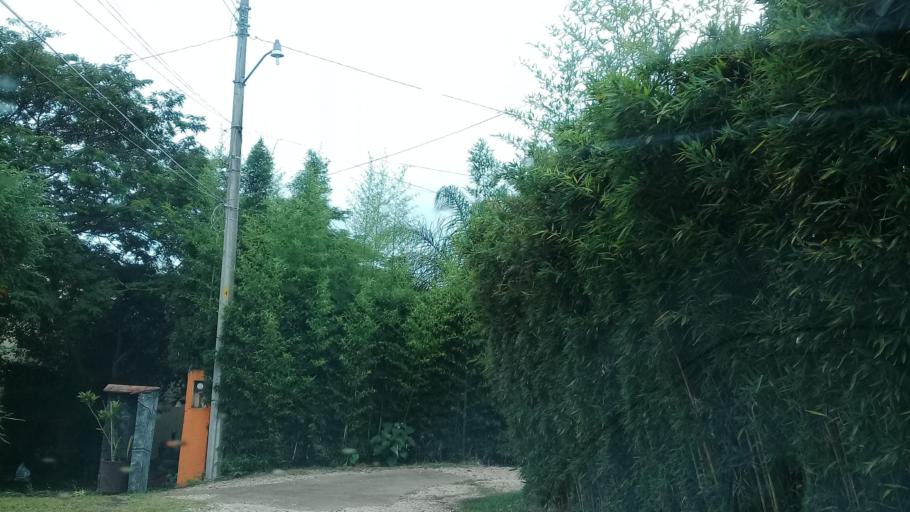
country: MX
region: Veracruz
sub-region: Emiliano Zapata
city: Jacarandas
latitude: 19.5063
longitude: -96.8380
